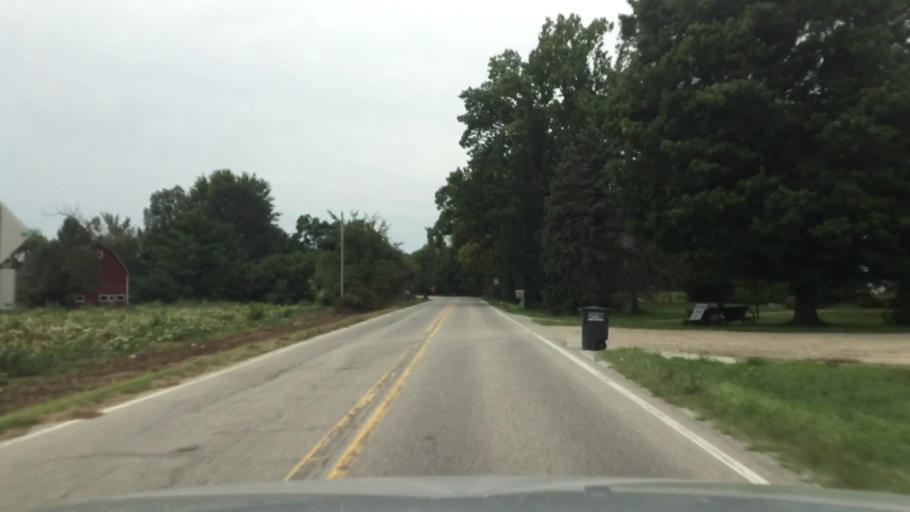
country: US
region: Michigan
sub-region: Washtenaw County
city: Milan
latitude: 42.1096
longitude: -83.7276
